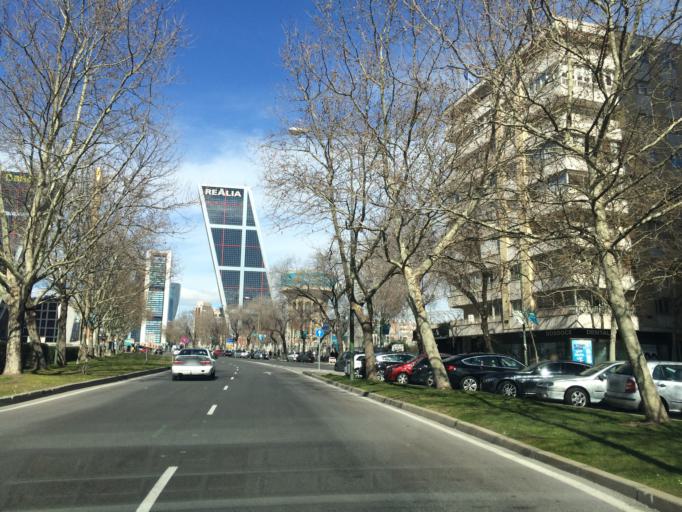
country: ES
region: Madrid
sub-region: Provincia de Madrid
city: Chamartin
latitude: 40.4631
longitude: -3.6893
